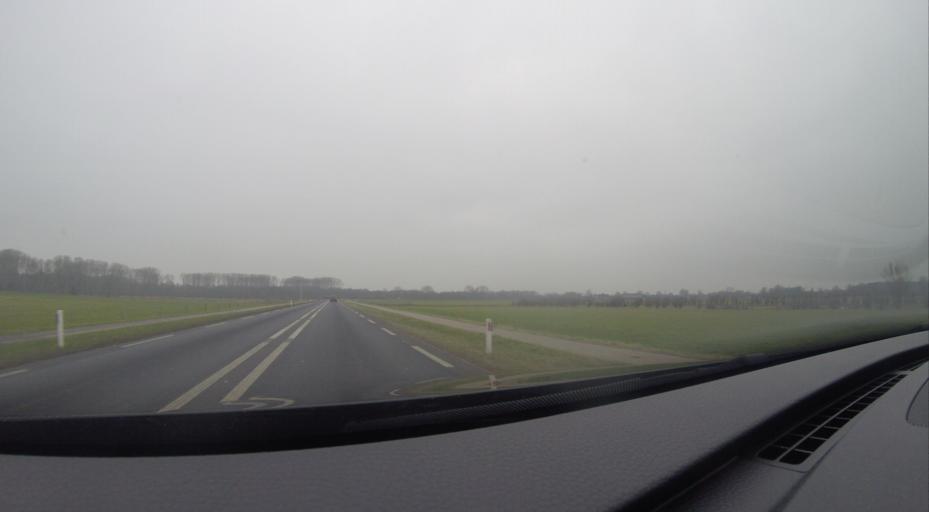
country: NL
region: Gelderland
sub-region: Gemeente Voorst
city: Voorst
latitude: 52.1480
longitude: 6.1541
